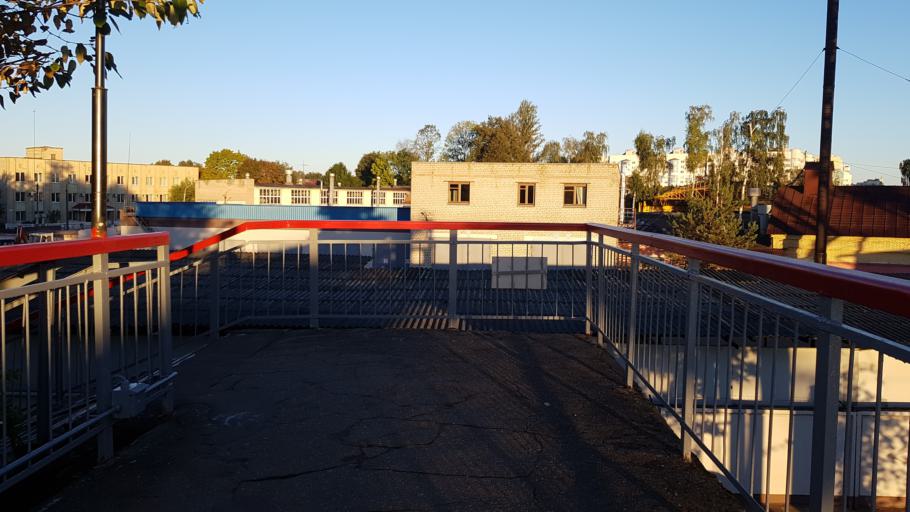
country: BY
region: Minsk
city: Syenitsa
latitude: 53.8777
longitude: 27.5238
